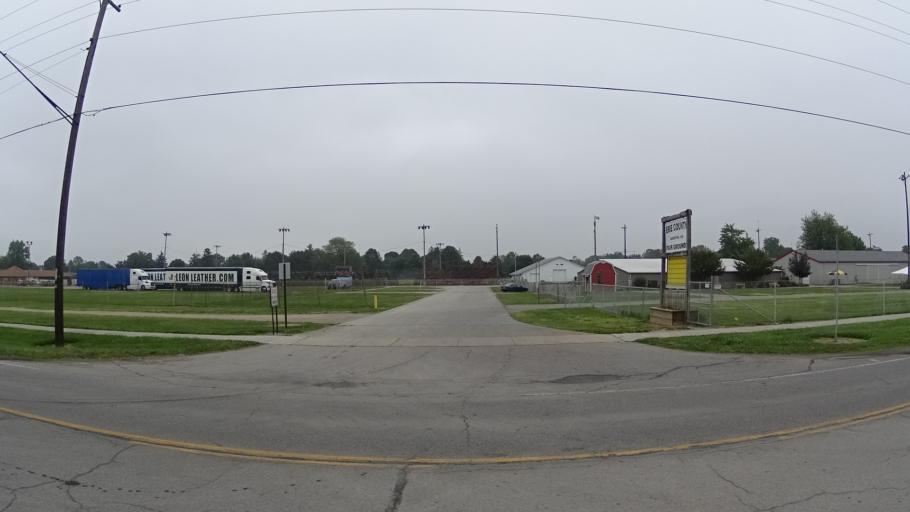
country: US
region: Ohio
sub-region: Erie County
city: Sandusky
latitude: 41.4251
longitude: -82.6935
